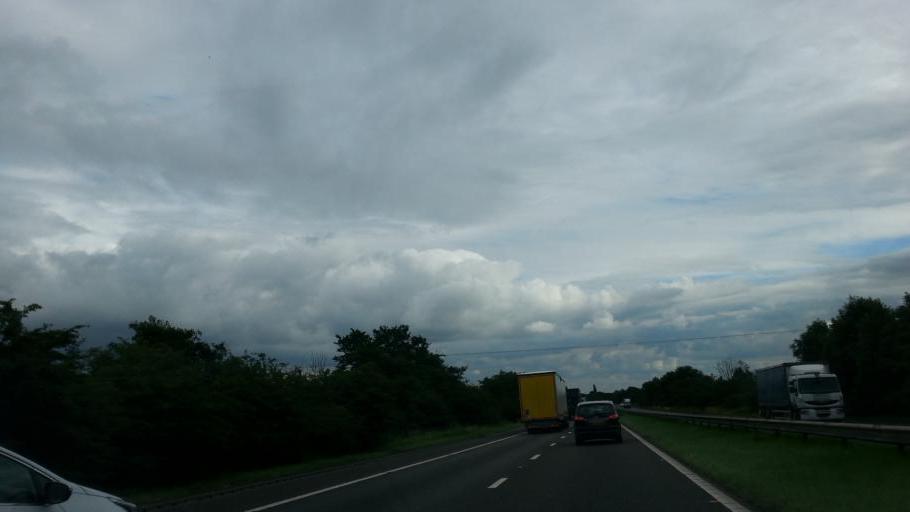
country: GB
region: England
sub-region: Doncaster
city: Tickhill
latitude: 53.4304
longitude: -1.0944
